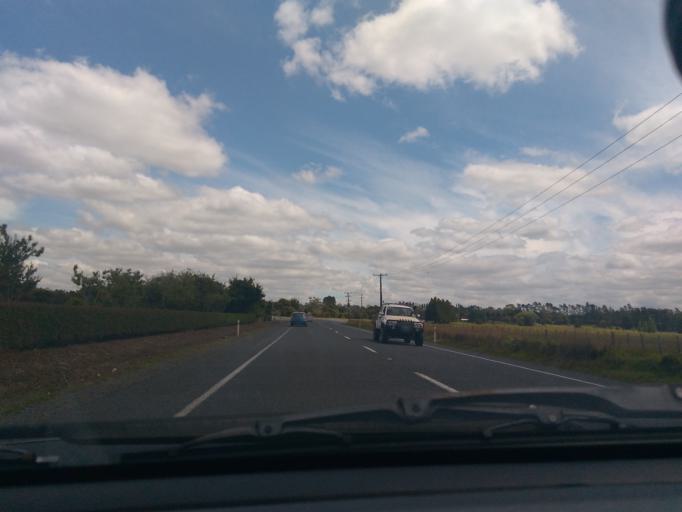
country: NZ
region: Northland
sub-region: Far North District
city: Kerikeri
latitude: -35.2277
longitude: 173.9199
